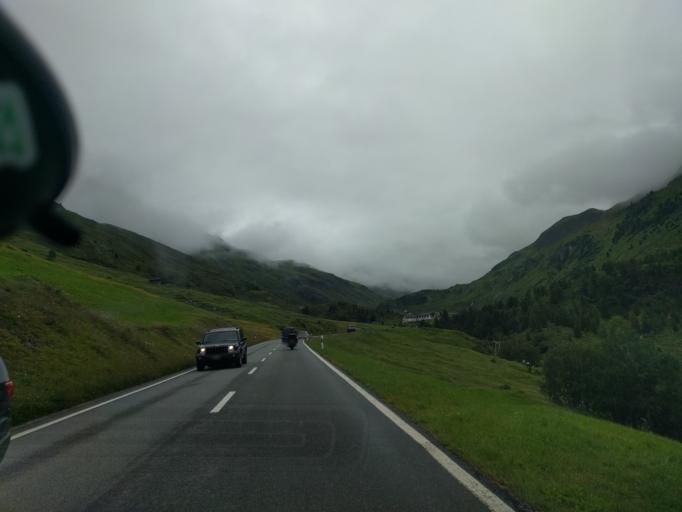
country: CH
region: Grisons
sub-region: Praettigau/Davos District
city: Davos
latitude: 46.7921
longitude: 9.9137
